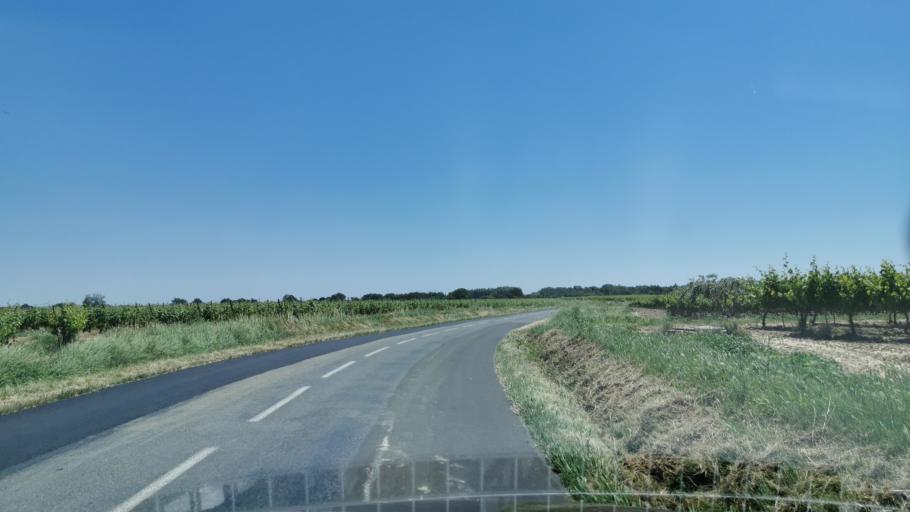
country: FR
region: Languedoc-Roussillon
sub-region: Departement de l'Aude
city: Moussan
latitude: 43.2545
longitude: 2.9605
